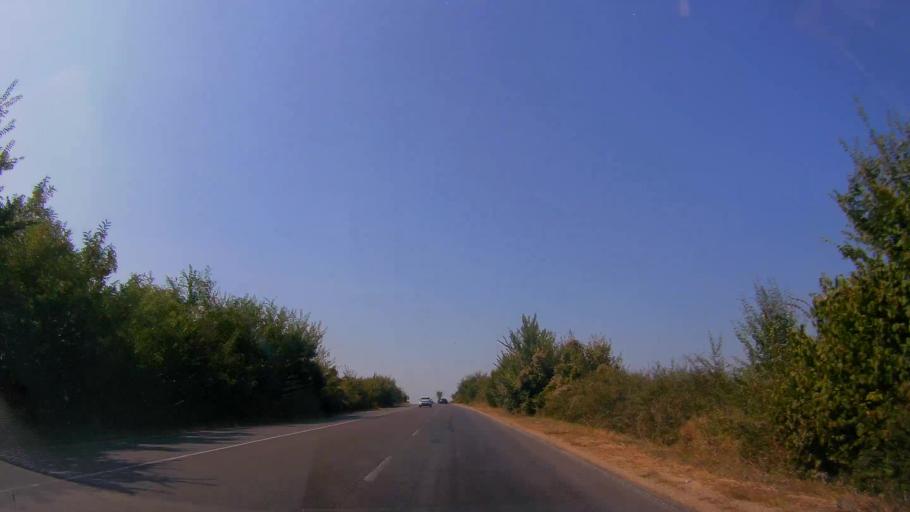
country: BG
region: Ruse
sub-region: Obshtina Vetovo
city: Senovo
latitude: 43.5618
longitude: 26.3634
